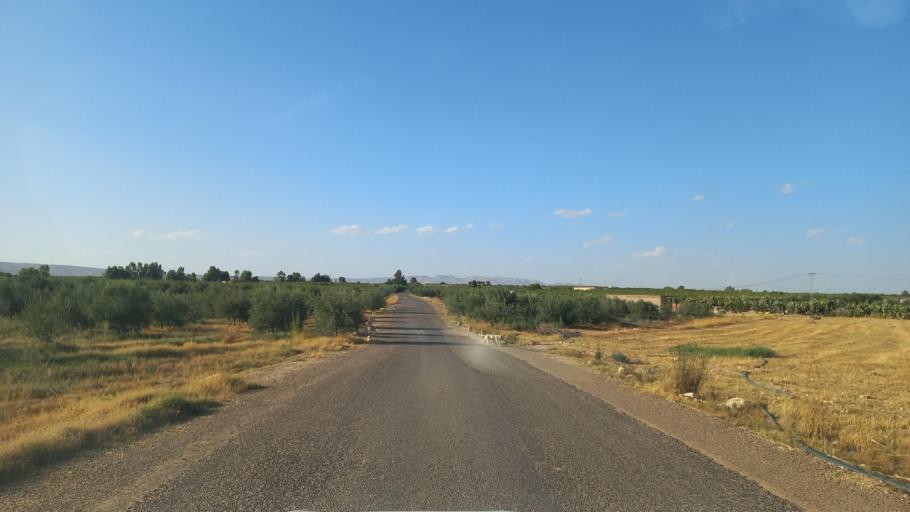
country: TN
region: Al Qasrayn
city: Kasserine
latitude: 35.2618
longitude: 9.0286
